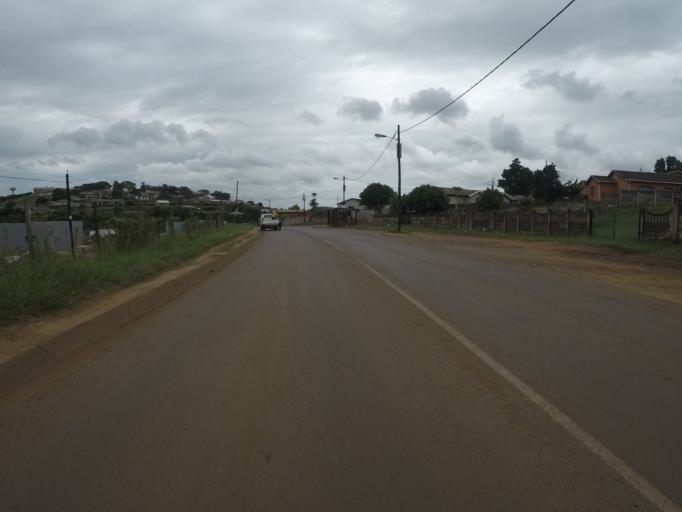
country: ZA
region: KwaZulu-Natal
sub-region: uThungulu District Municipality
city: Empangeni
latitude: -28.7829
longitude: 31.8609
